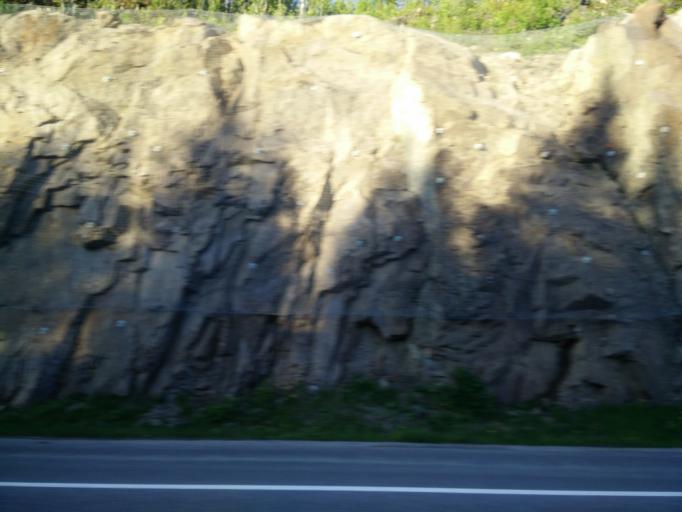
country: NO
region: Akershus
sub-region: Baerum
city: Skui
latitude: 59.9678
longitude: 10.3409
